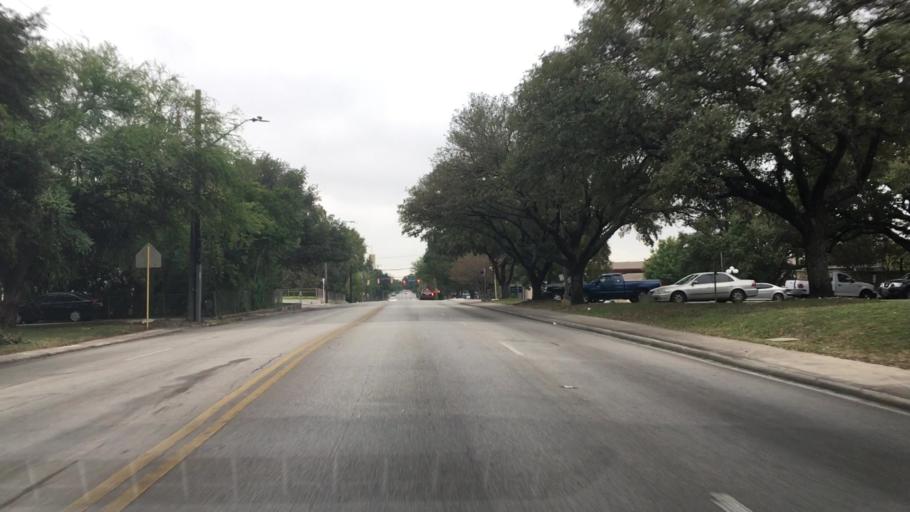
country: US
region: Texas
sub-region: Bexar County
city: Balcones Heights
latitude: 29.4751
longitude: -98.5480
